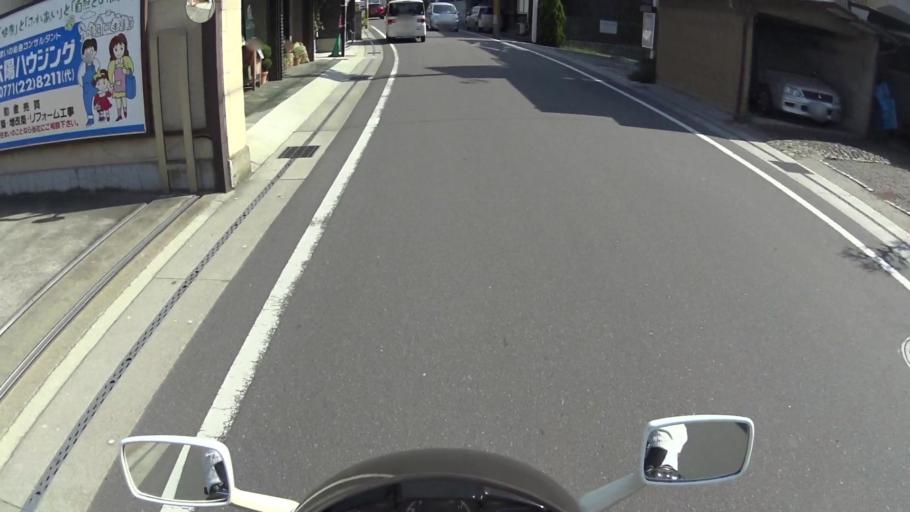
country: JP
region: Kyoto
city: Kameoka
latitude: 35.0076
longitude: 135.5837
